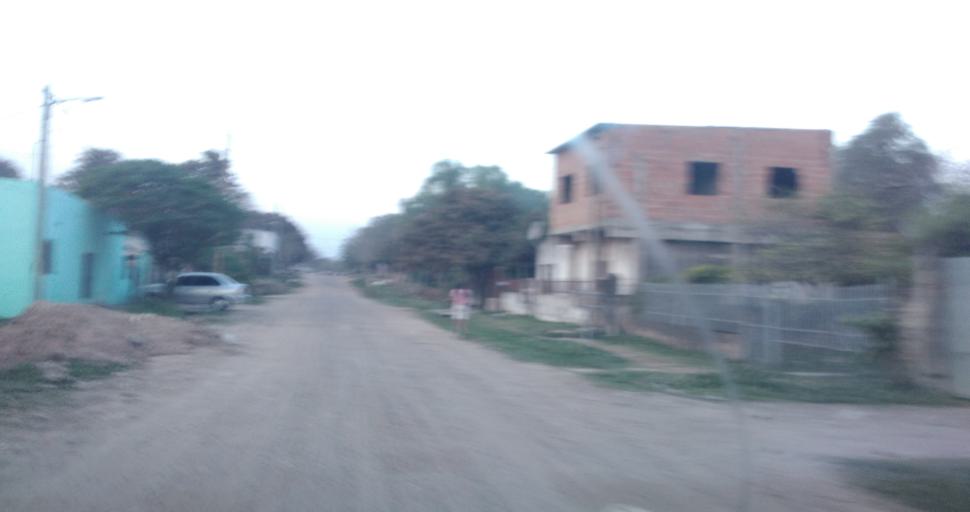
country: AR
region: Chaco
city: Fontana
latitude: -27.4295
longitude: -59.0064
